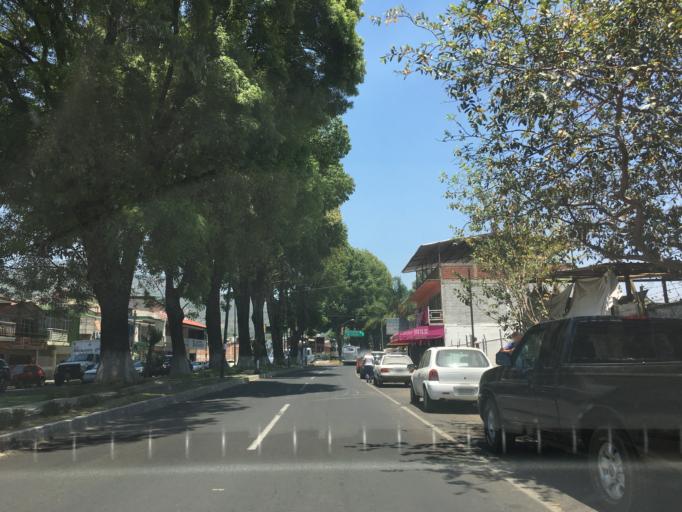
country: MX
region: Michoacan
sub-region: Uruapan
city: Uruapan
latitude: 19.4189
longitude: -102.0499
